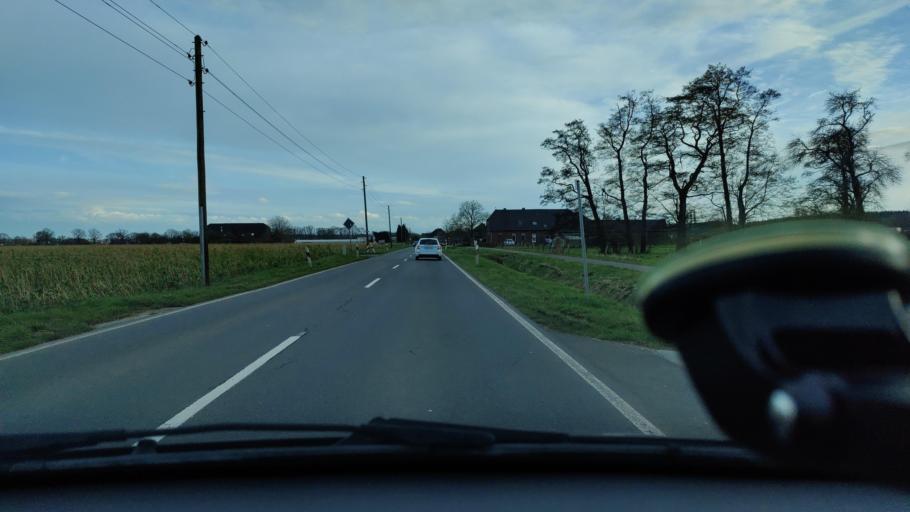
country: DE
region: North Rhine-Westphalia
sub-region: Regierungsbezirk Dusseldorf
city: Alpen
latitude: 51.5998
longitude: 6.4599
